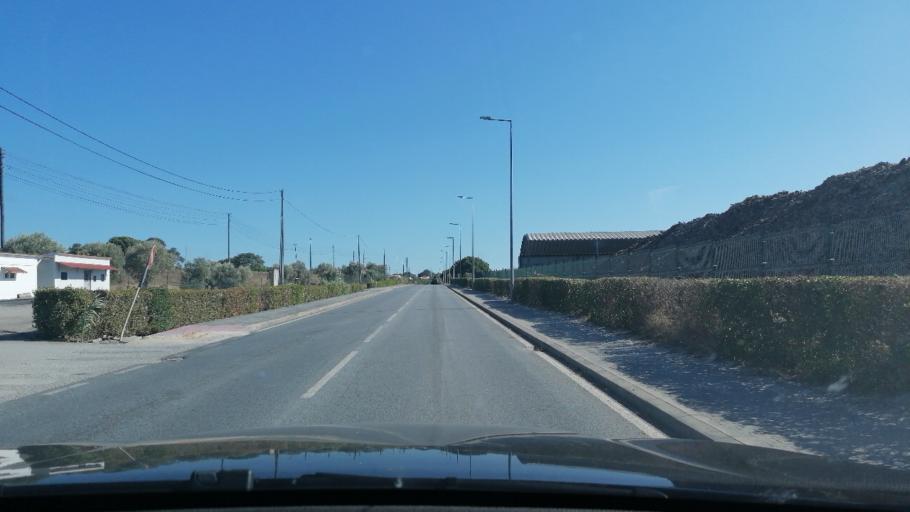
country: PT
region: Setubal
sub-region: Alcacer do Sal
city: Alcacer do Sal
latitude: 38.3913
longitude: -8.5135
